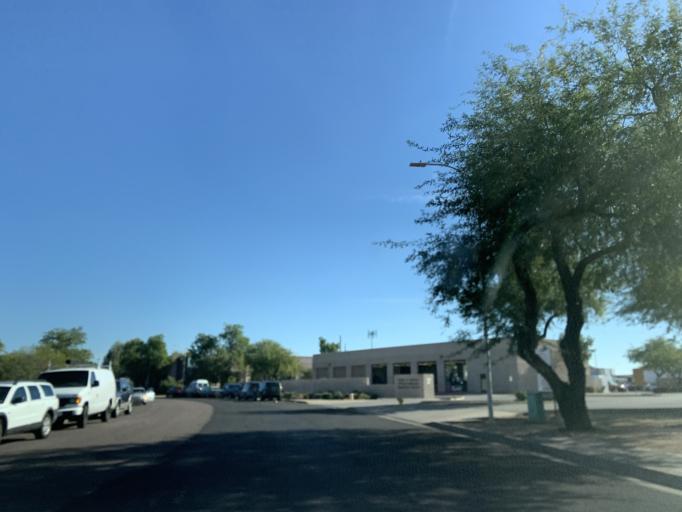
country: US
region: Arizona
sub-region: Maricopa County
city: Tempe
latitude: 33.4125
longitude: -111.8727
